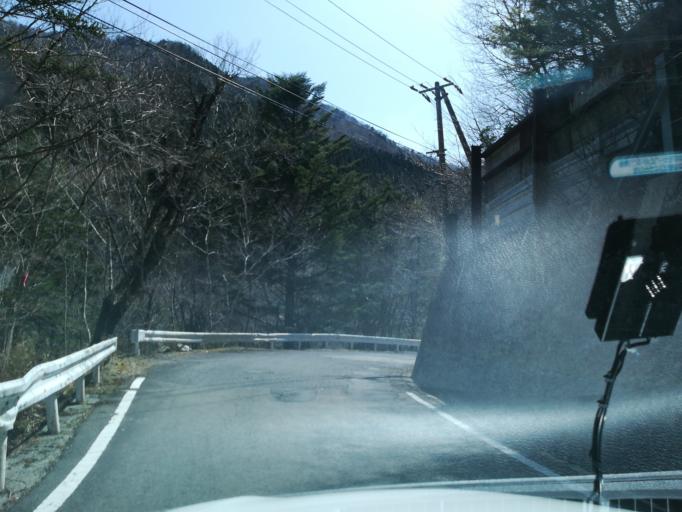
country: JP
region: Tokushima
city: Wakimachi
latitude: 33.8581
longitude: 134.0538
